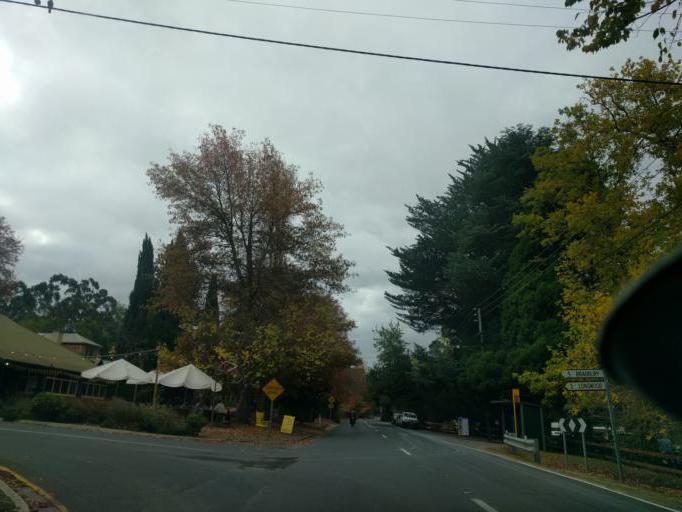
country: AU
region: South Australia
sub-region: Adelaide Hills
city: Stirling
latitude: -35.0427
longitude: 138.7601
